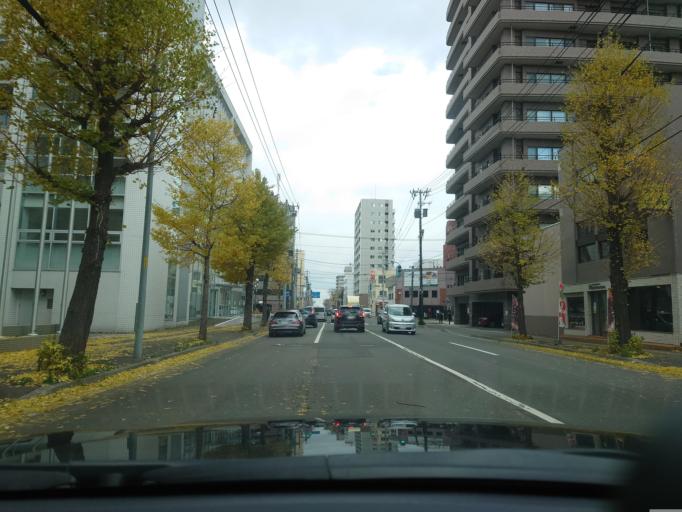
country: JP
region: Hokkaido
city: Sapporo
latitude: 43.0549
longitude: 141.3277
